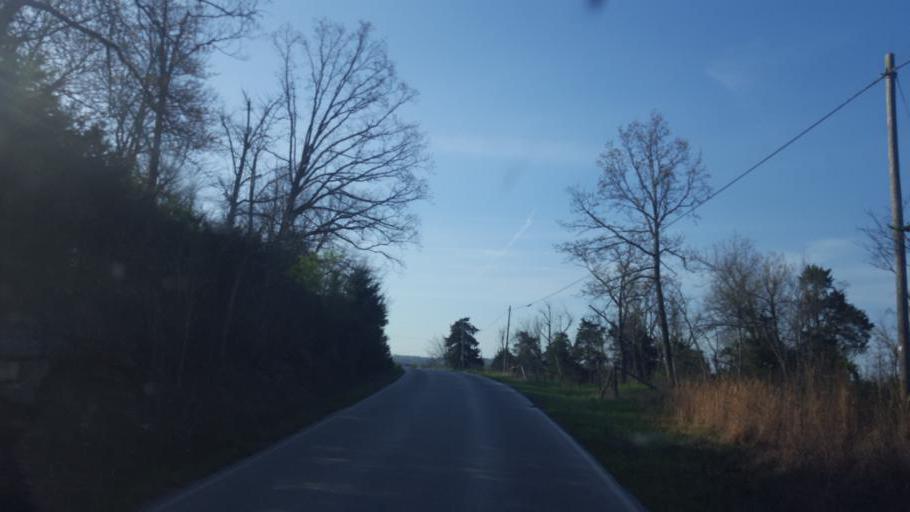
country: US
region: Kentucky
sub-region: Larue County
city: Hodgenville
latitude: 37.4817
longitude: -85.9262
